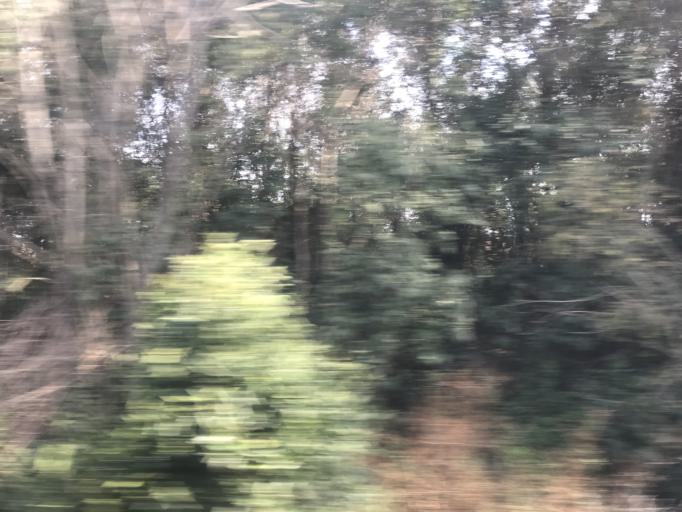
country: AR
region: Cordoba
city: Laguna Larga
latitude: -31.7878
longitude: -63.7937
